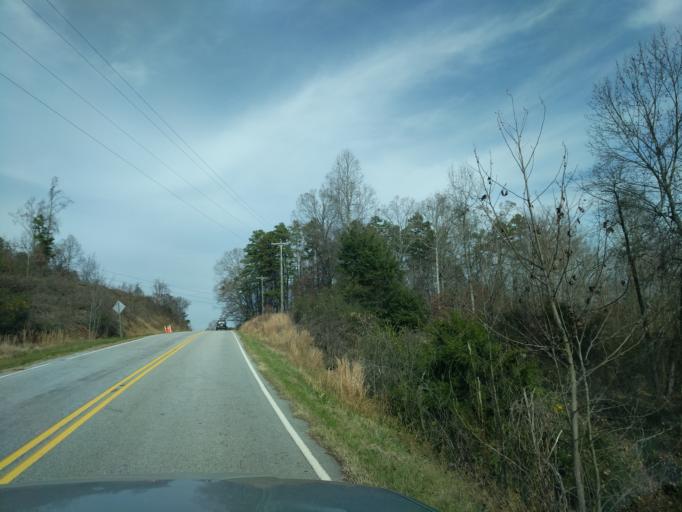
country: US
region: South Carolina
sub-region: Oconee County
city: Utica
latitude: 34.7793
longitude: -82.9066
